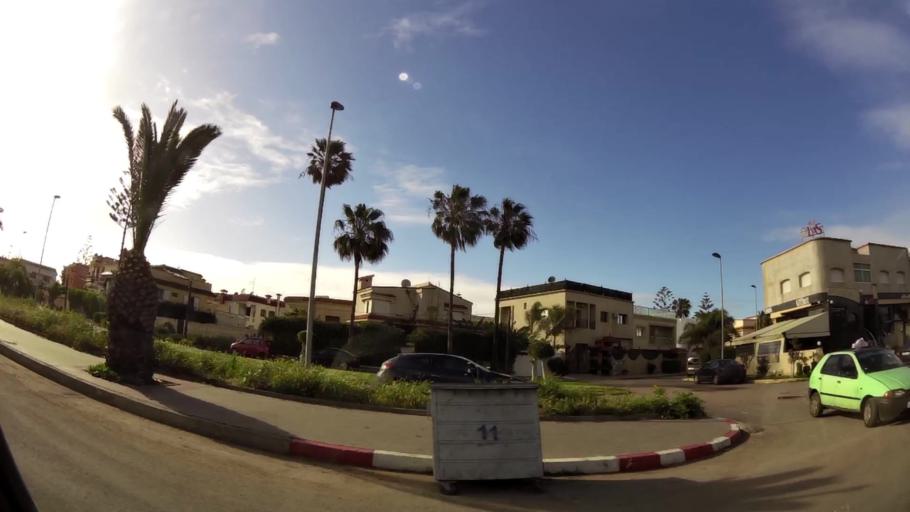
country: MA
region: Grand Casablanca
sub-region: Mohammedia
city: Mohammedia
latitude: 33.7078
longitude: -7.3613
